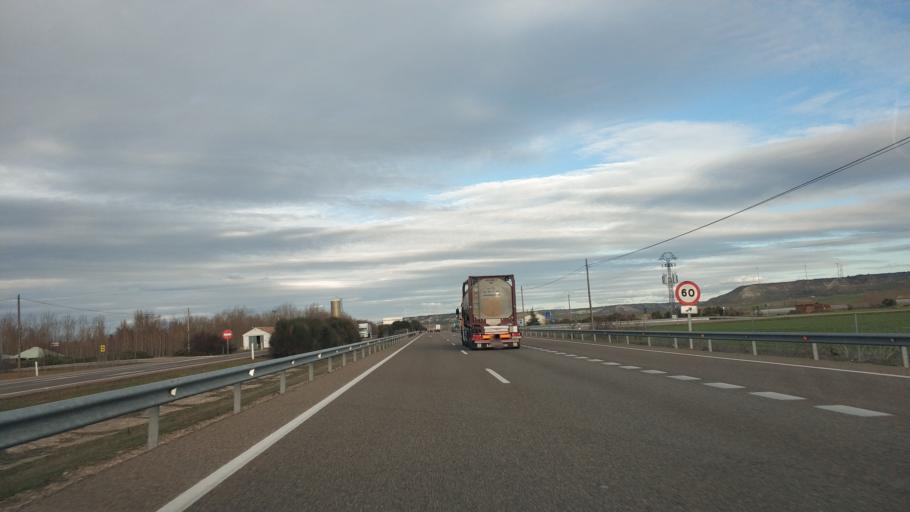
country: ES
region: Castille and Leon
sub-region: Provincia de Palencia
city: Torquemada
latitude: 42.0291
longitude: -4.3118
